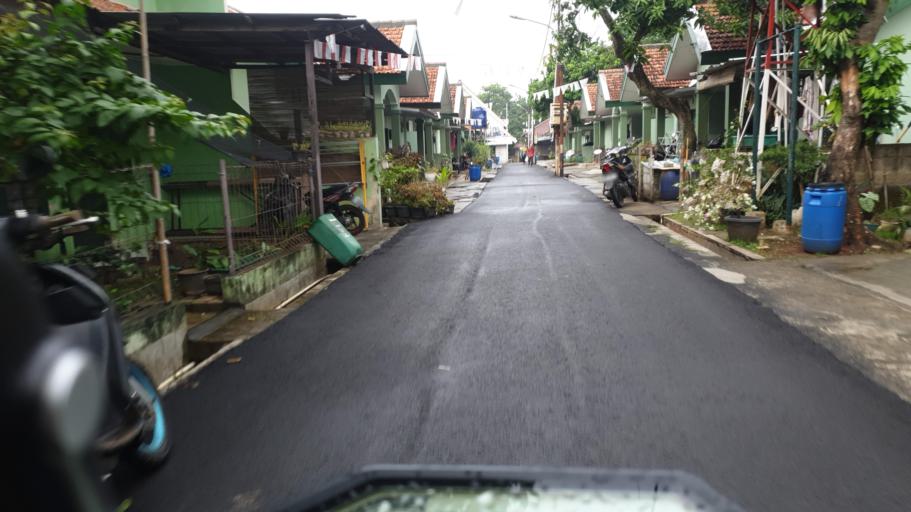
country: ID
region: West Java
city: Depok
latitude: -6.3413
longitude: 106.8322
